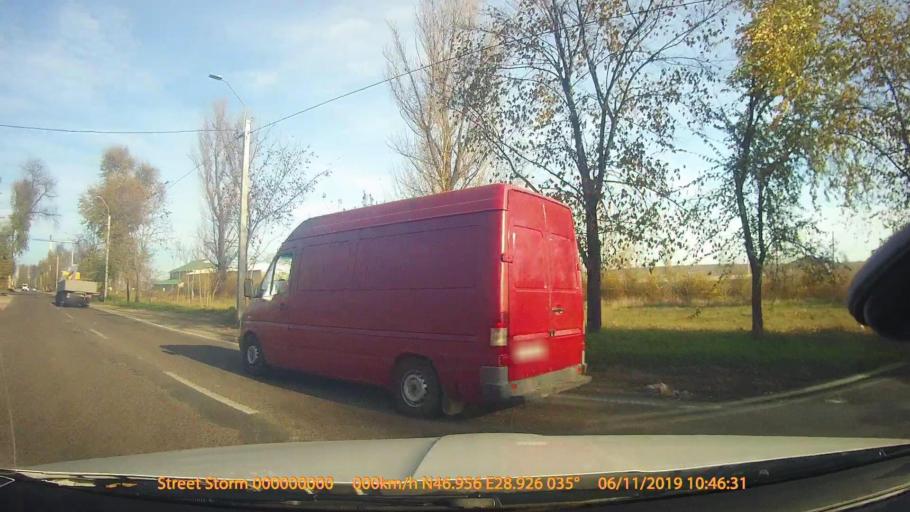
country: MD
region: Chisinau
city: Singera
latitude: 46.9560
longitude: 28.9262
